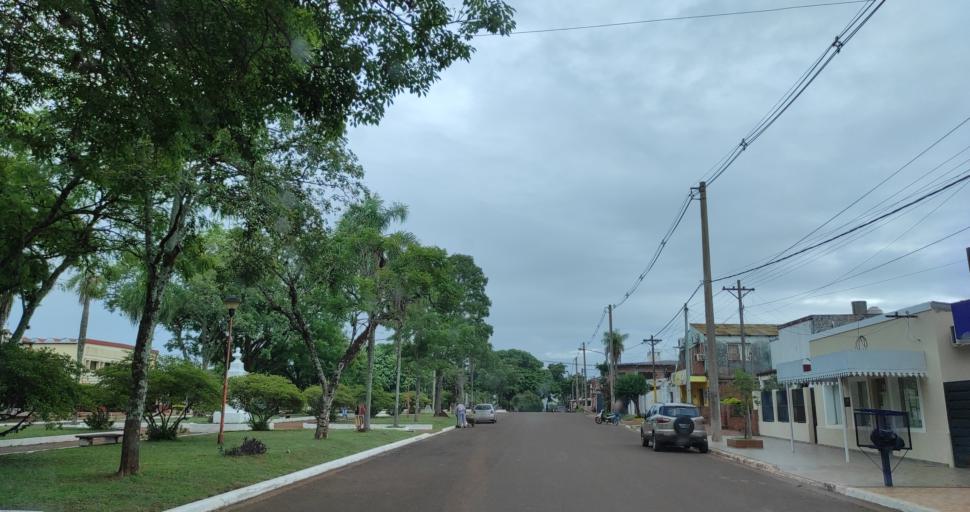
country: AR
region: Misiones
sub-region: Departamento de Apostoles
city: San Jose
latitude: -27.7691
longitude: -55.7791
